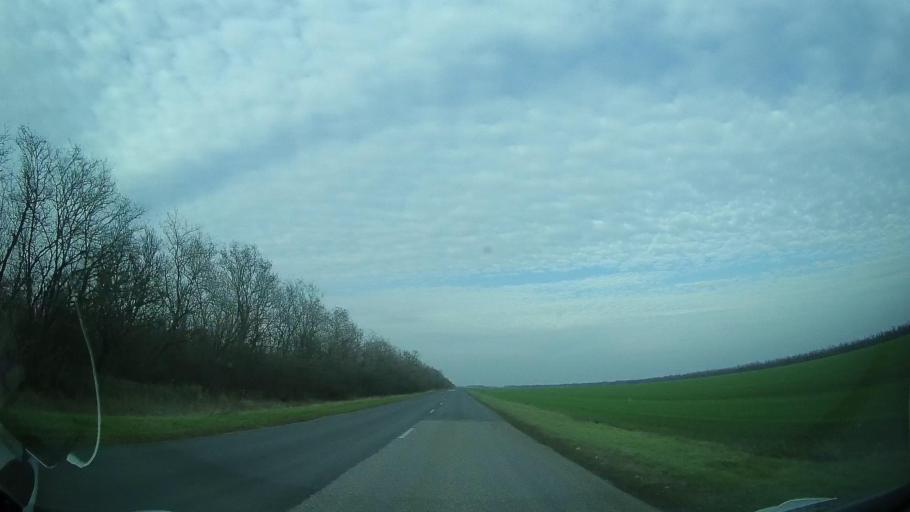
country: RU
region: Rostov
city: Zernograd
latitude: 46.9456
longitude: 40.3666
